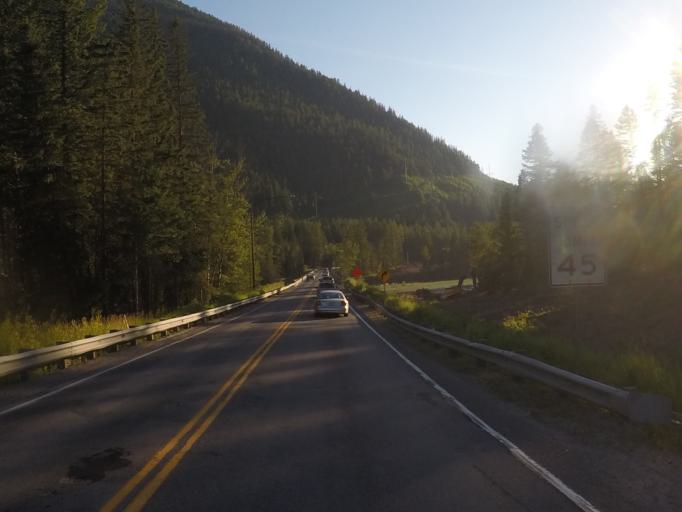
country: US
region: Montana
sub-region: Flathead County
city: Columbia Falls
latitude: 48.3852
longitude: -114.0762
